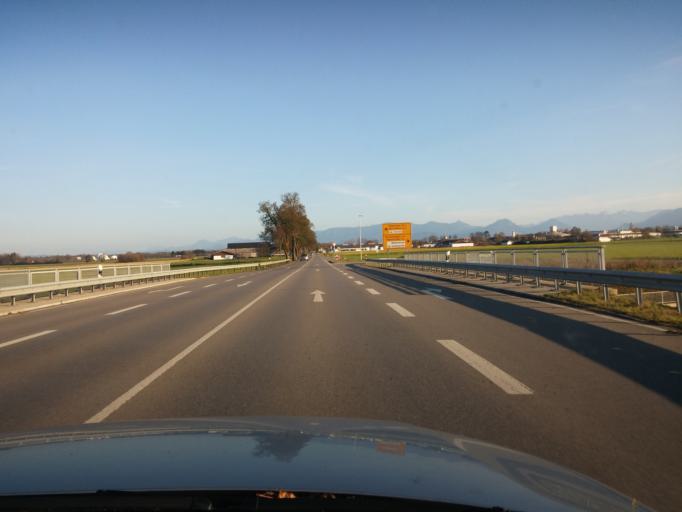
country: DE
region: Bavaria
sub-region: Upper Bavaria
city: Bruckmuhl
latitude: 47.8820
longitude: 11.9554
